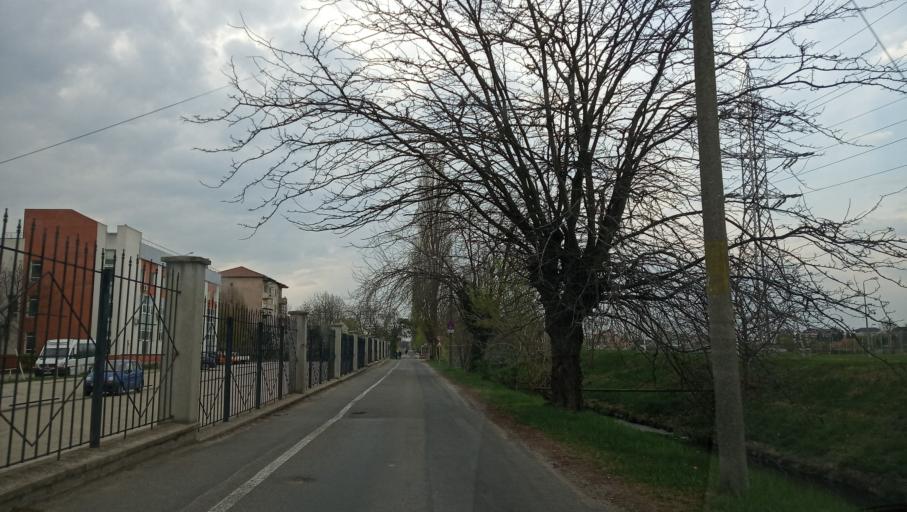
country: RO
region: Bihor
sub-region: Comuna Biharea
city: Oradea
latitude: 47.0460
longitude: 21.9202
